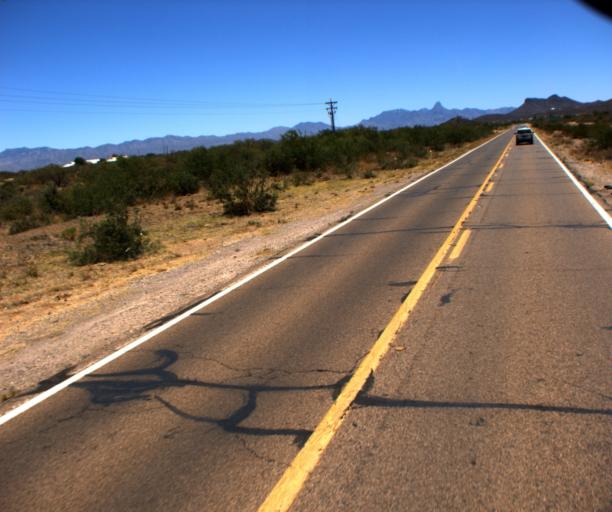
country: US
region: Arizona
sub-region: Pima County
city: Sells
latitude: 31.9291
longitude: -111.9050
